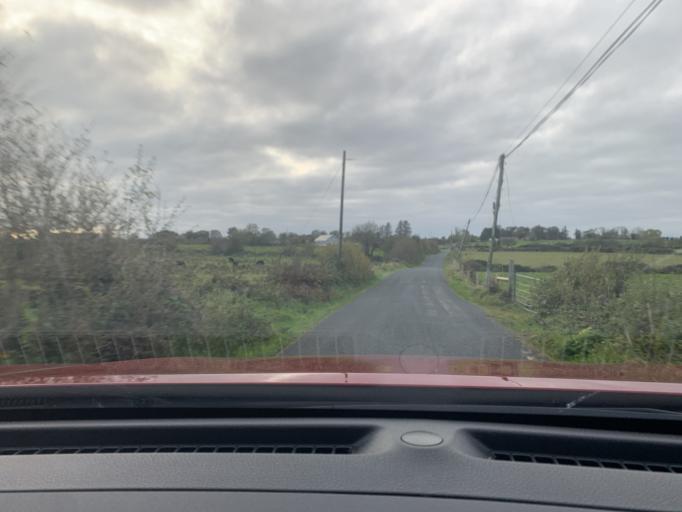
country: IE
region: Connaught
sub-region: Sligo
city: Tobercurry
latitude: 54.0286
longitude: -8.6893
